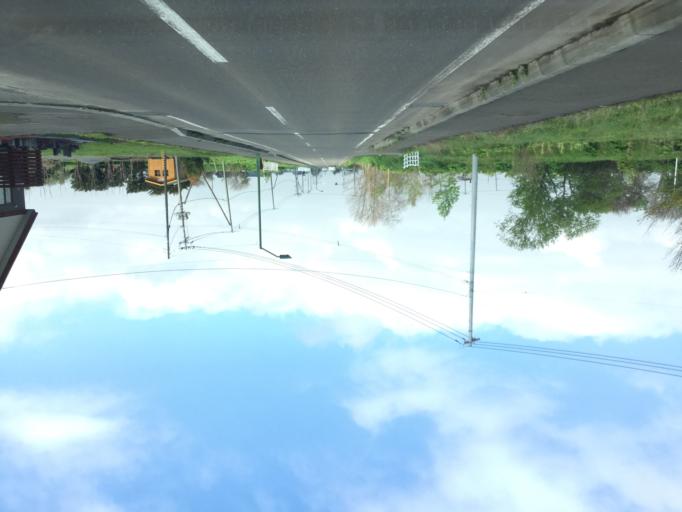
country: JP
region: Hokkaido
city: Iwamizawa
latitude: 43.1637
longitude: 141.7460
